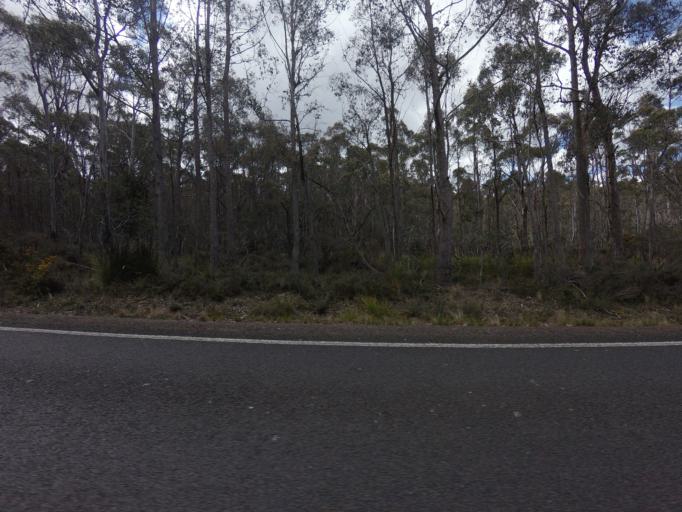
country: AU
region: Tasmania
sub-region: Northern Midlands
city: Evandale
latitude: -42.0129
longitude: 147.7298
